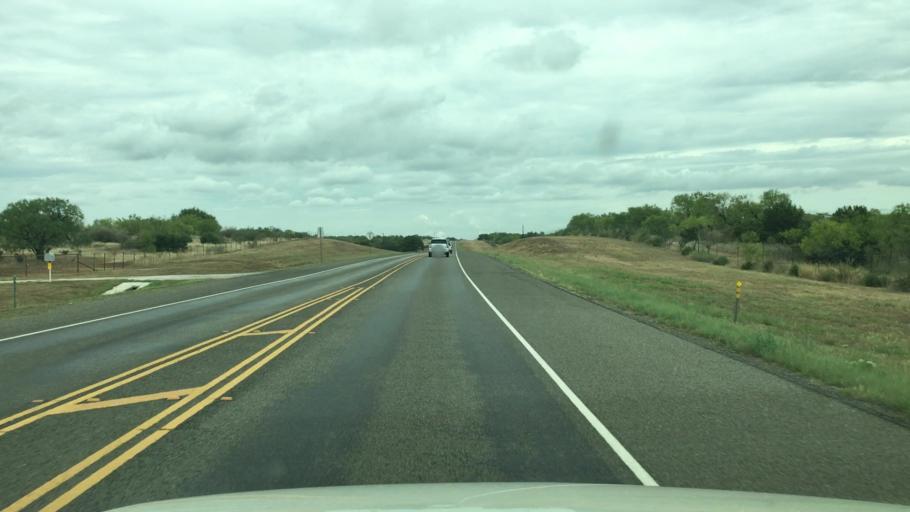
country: US
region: Texas
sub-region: Llano County
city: Kingsland
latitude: 30.5711
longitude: -98.4877
